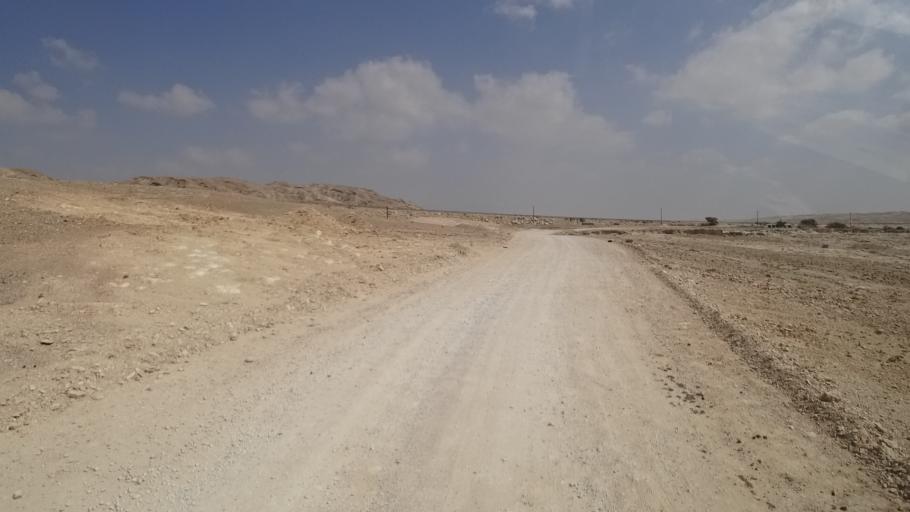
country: OM
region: Zufar
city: Salalah
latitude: 17.2421
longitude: 53.9119
